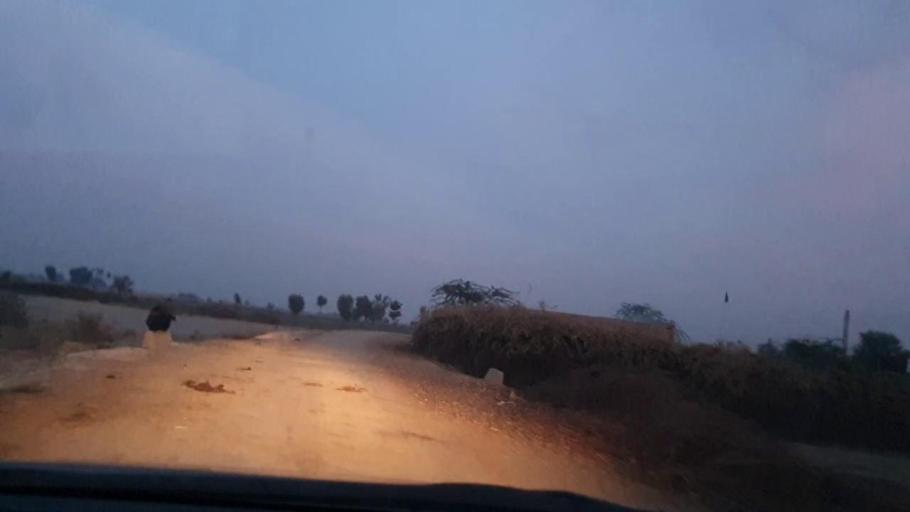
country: PK
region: Sindh
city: Sakrand
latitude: 26.1870
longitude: 68.3026
